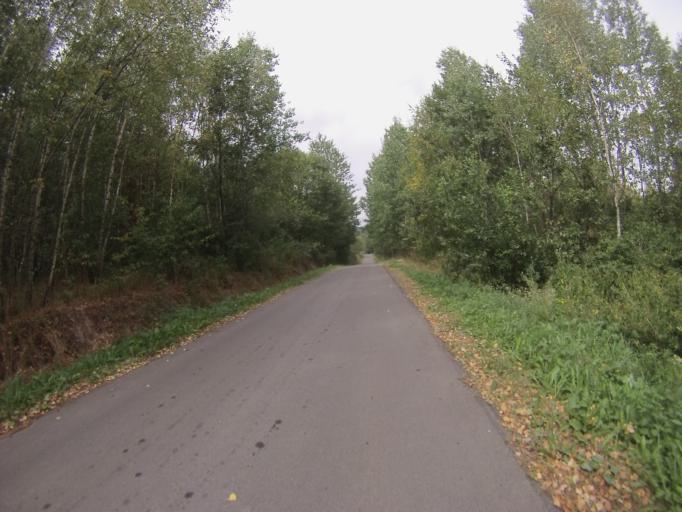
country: PL
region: Swietokrzyskie
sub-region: Powiat kielecki
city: Lagow
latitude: 50.7629
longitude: 21.1055
